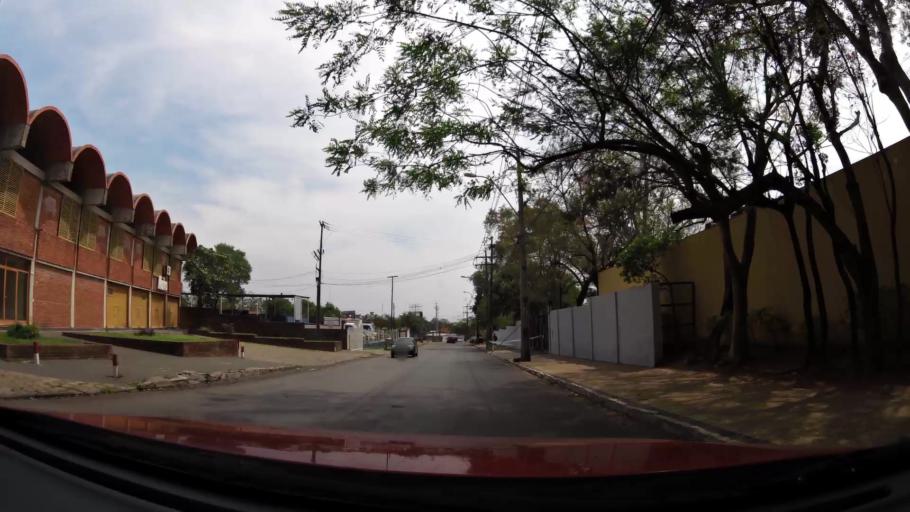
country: PY
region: Asuncion
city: Asuncion
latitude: -25.2648
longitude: -57.5934
